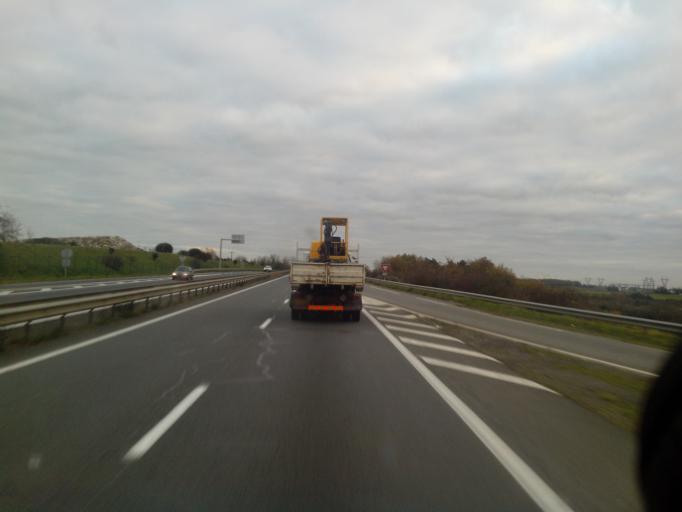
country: FR
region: Poitou-Charentes
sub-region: Departement de la Vienne
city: Montamise
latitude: 46.6100
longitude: 0.3897
